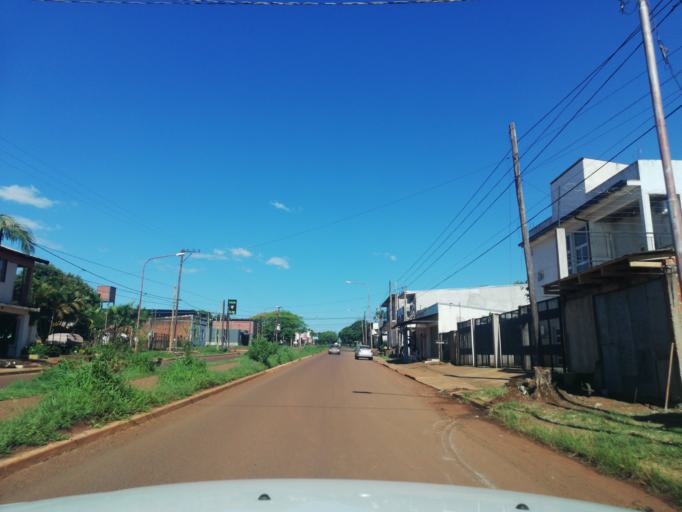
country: AR
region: Misiones
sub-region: Departamento de Capital
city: Posadas
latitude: -27.3987
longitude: -55.9237
